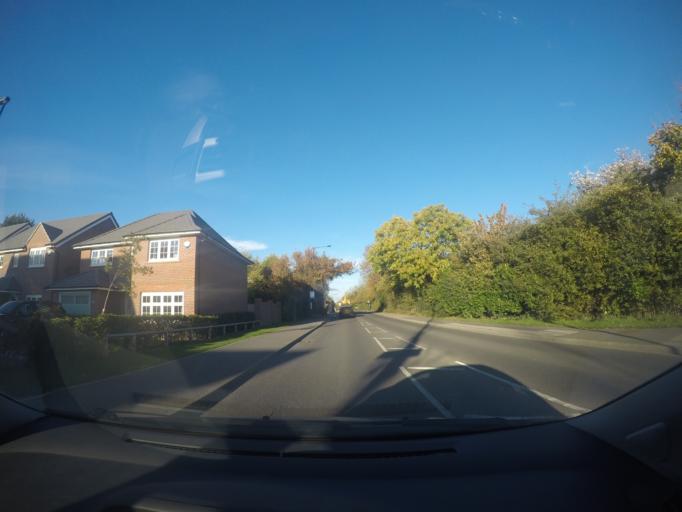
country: GB
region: England
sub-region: City of York
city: York
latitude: 53.9814
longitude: -1.0948
